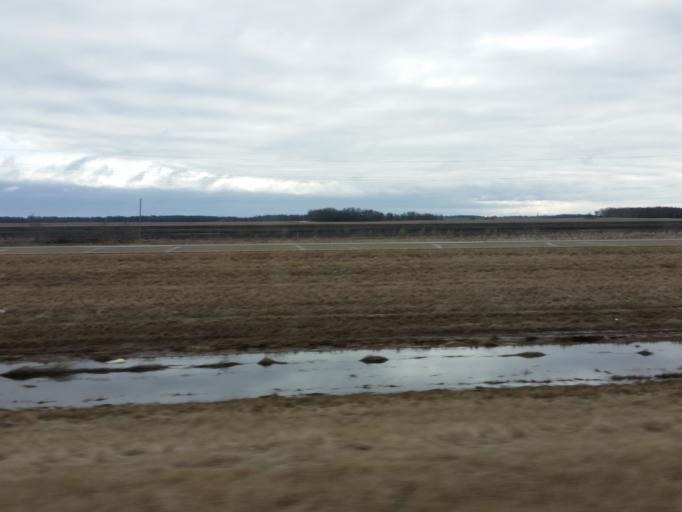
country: US
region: North Dakota
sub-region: Walsh County
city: Grafton
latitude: 48.2705
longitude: -97.1892
